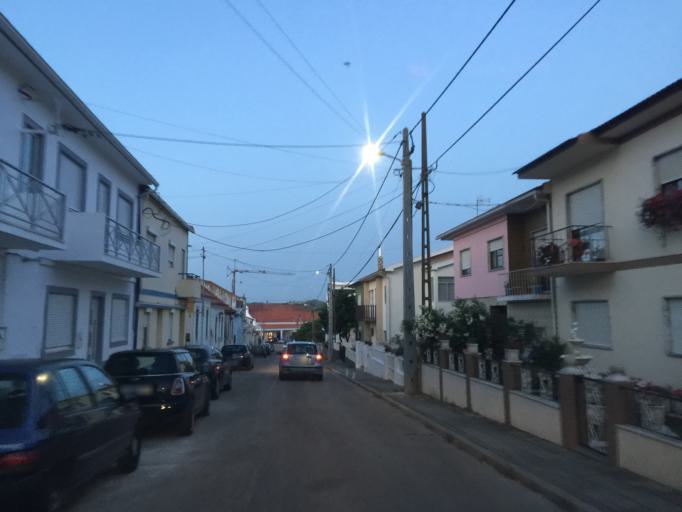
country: PT
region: Leiria
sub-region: Bombarral
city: Bombarral
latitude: 39.2640
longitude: -9.1567
